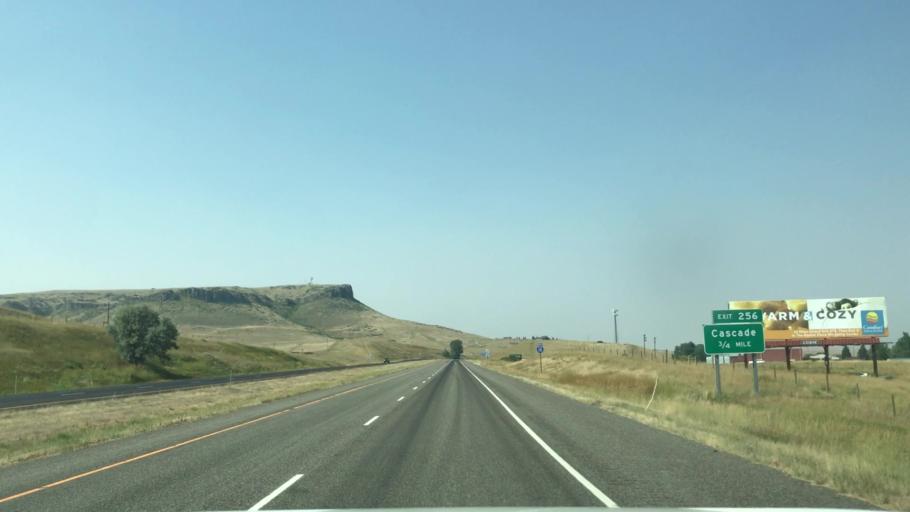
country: US
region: Montana
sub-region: Cascade County
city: Sun Prairie
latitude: 47.2668
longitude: -111.7079
